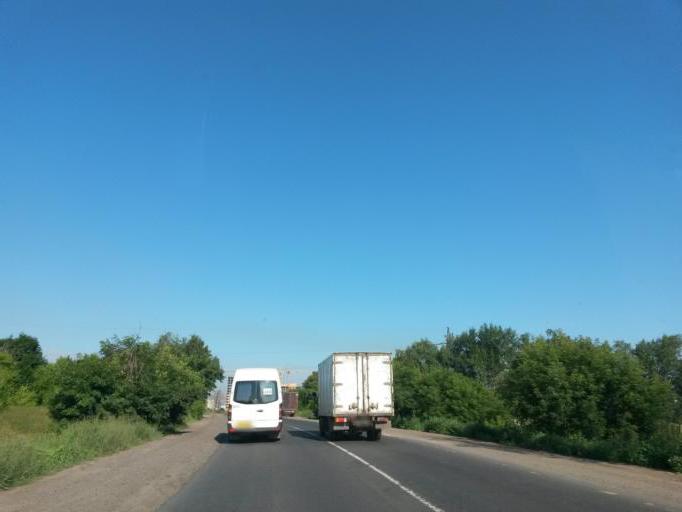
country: RU
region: Moskovskaya
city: Razvilka
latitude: 55.5809
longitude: 37.7539
